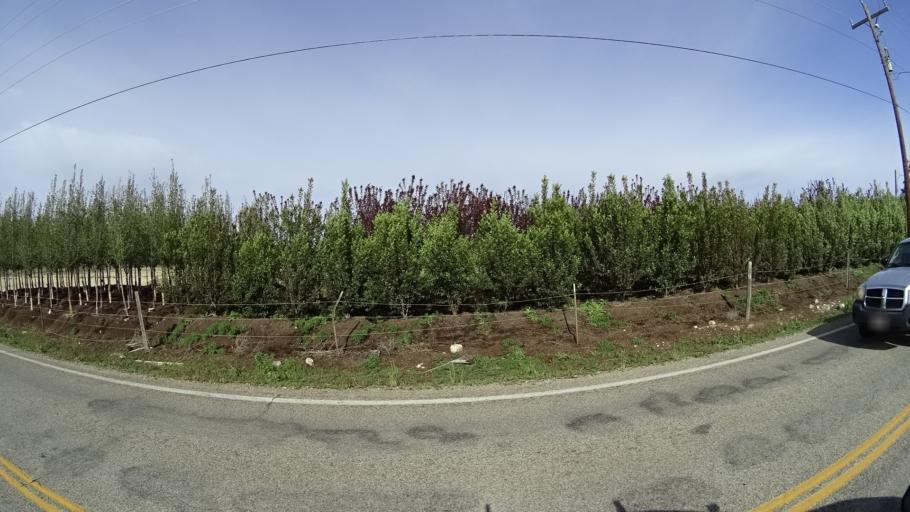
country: US
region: Idaho
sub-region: Ada County
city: Kuna
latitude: 43.4818
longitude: -116.3345
